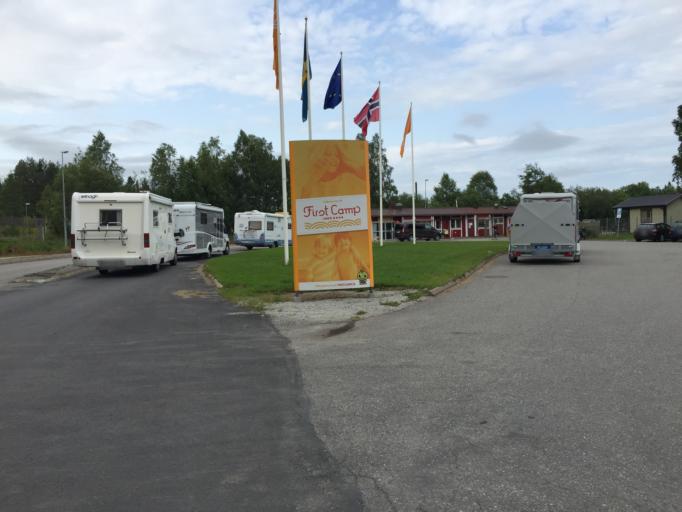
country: SE
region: Vaesterbotten
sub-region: Umea Kommun
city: Ersmark
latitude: 63.8426
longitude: 20.3402
